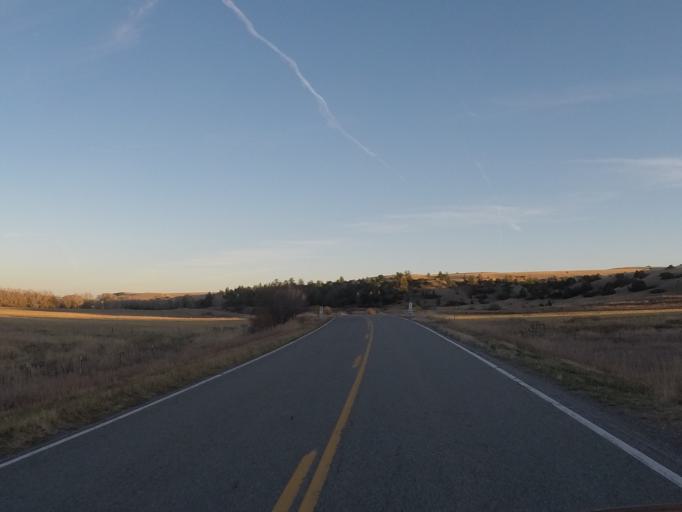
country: US
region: Montana
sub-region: Sweet Grass County
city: Big Timber
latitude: 45.7875
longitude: -109.8505
